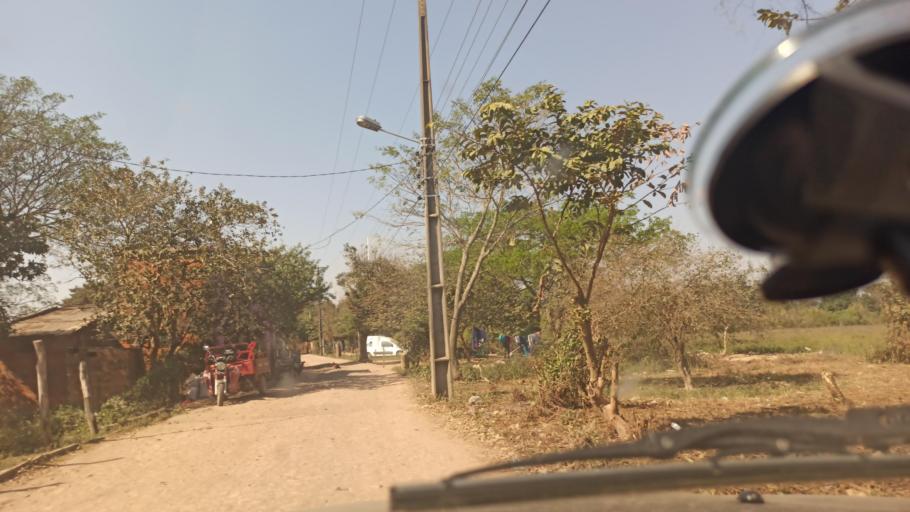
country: AR
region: Formosa
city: Clorinda
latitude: -25.2958
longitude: -57.7024
